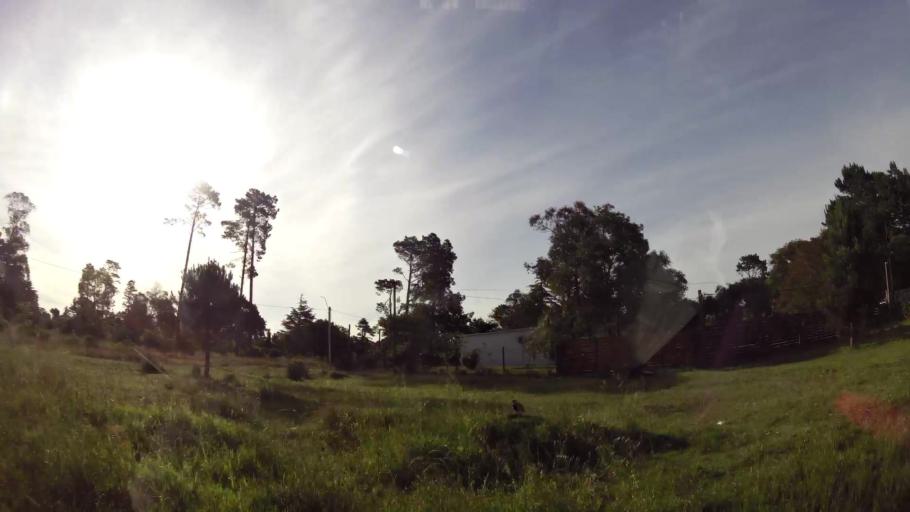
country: UY
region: Canelones
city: Empalme Olmos
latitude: -34.7827
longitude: -55.8546
